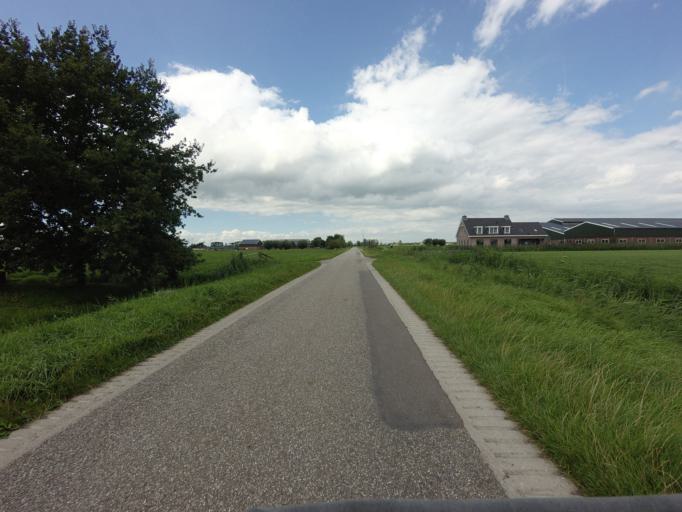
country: NL
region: Utrecht
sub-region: Gemeente Montfoort
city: Montfoort
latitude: 52.0368
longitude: 4.9981
